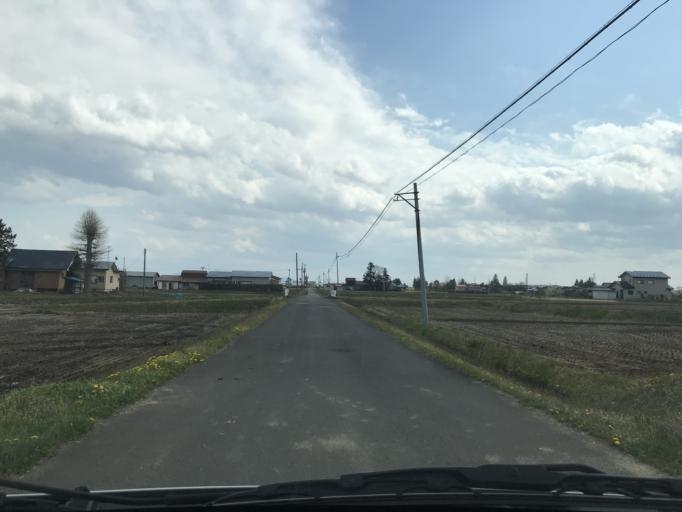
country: JP
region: Iwate
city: Mizusawa
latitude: 39.1784
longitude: 141.1256
